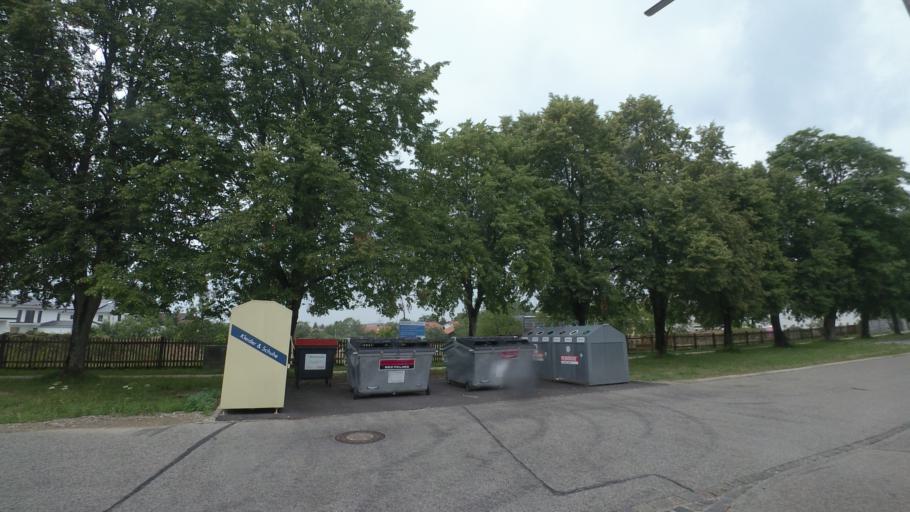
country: DE
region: Bavaria
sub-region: Upper Bavaria
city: Traunstein
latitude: 47.8621
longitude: 12.6326
